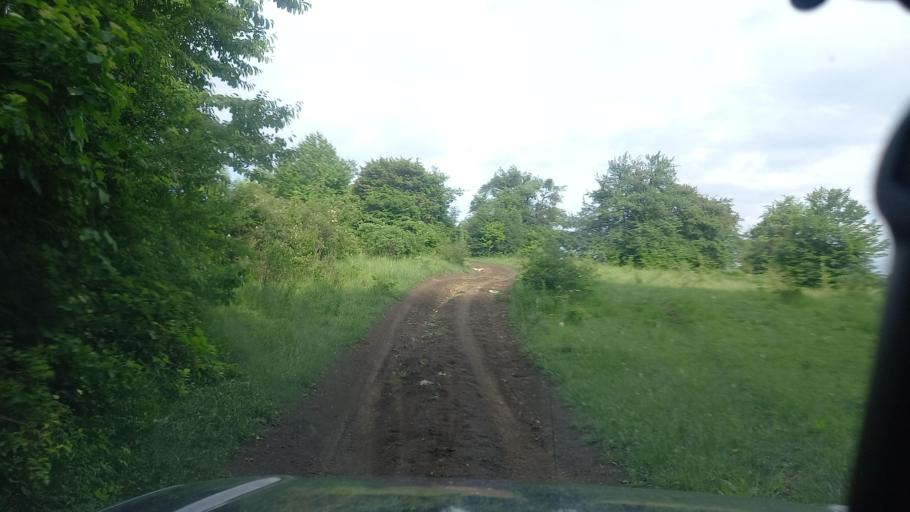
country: RU
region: Karachayevo-Cherkesiya
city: Kurdzhinovo
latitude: 44.1267
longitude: 41.0727
